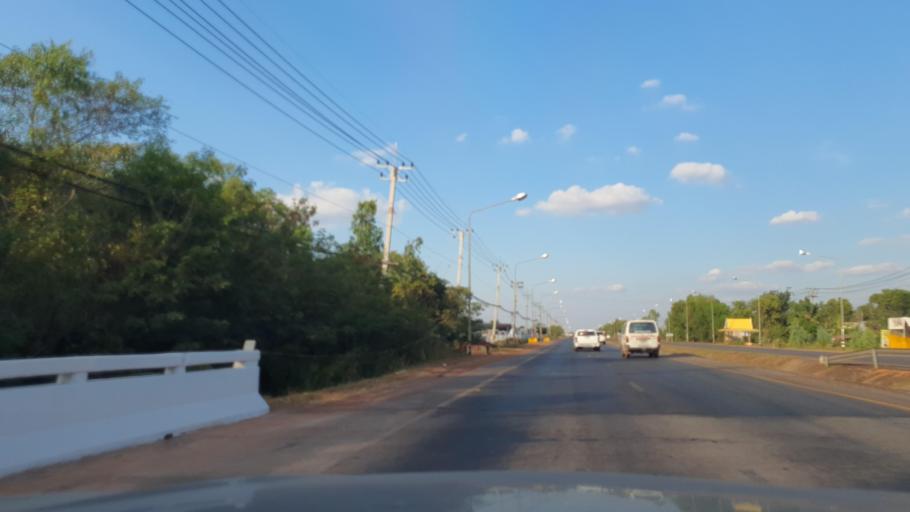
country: TH
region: Sakon Nakhon
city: Sakon Nakhon
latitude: 17.2313
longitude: 104.1077
